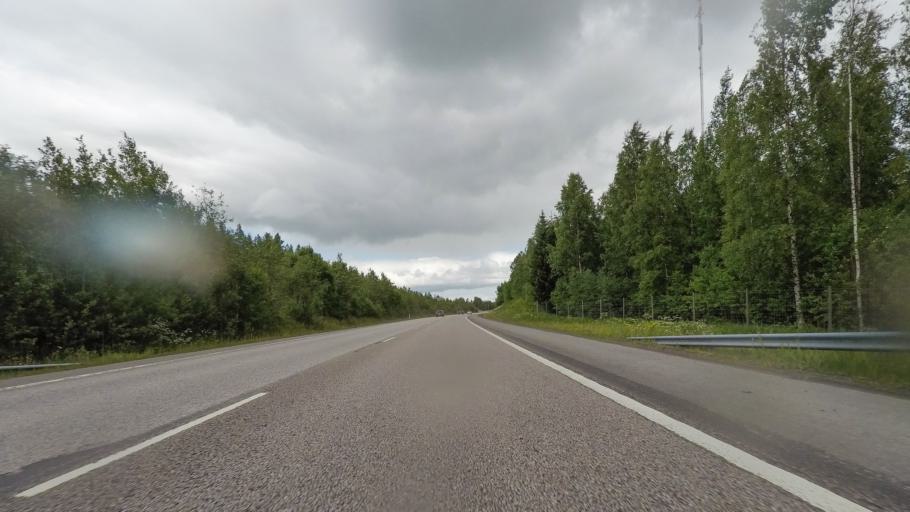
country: FI
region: Uusimaa
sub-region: Porvoo
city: Pukkila
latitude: 60.8191
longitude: 25.5165
